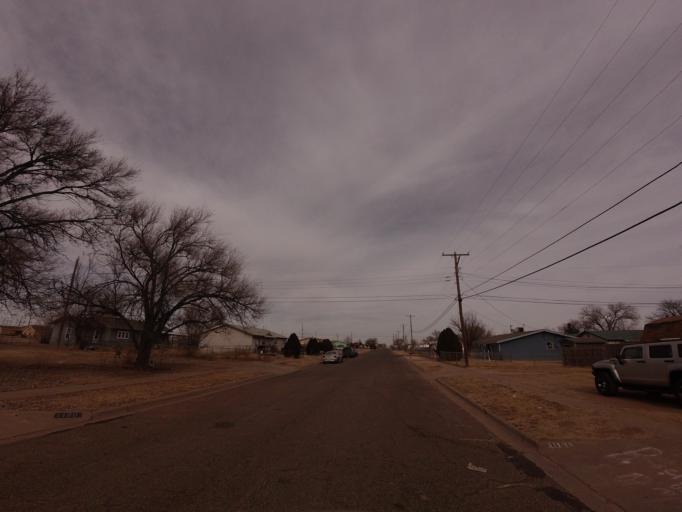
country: US
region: New Mexico
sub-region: Curry County
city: Clovis
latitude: 34.4092
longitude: -103.2447
